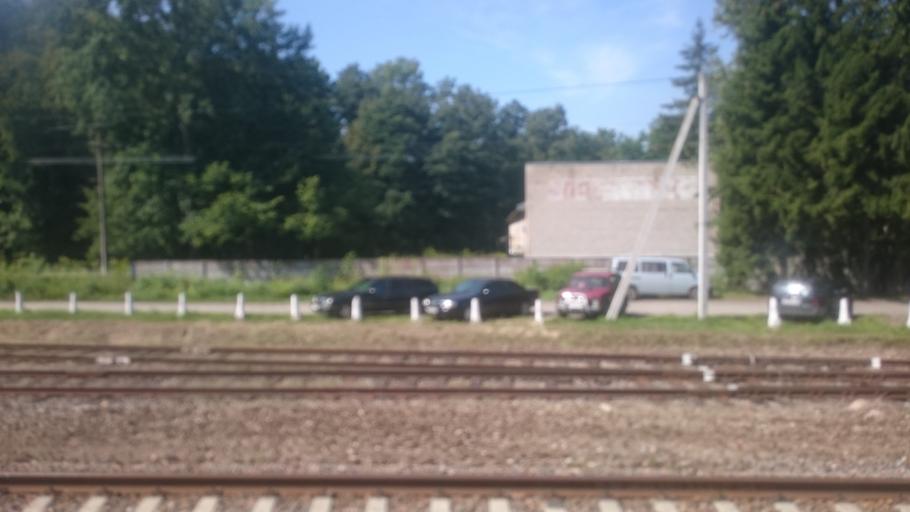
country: RU
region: Kaliningrad
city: Gur'yevsk
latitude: 54.8283
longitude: 20.5071
